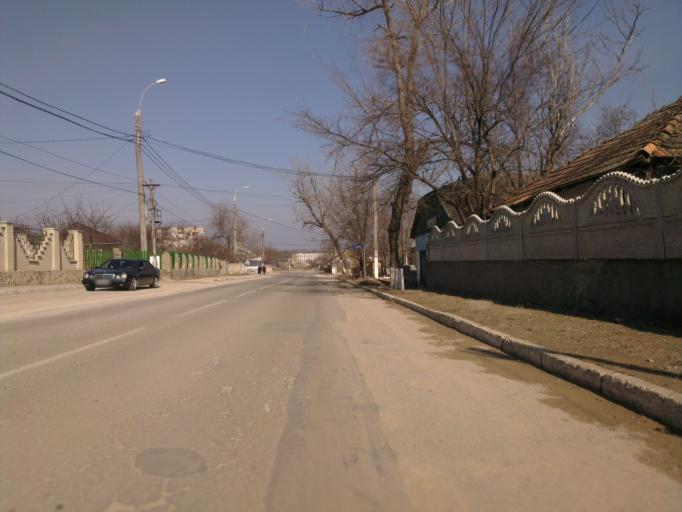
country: MD
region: Chisinau
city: Cricova
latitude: 47.1355
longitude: 28.8670
